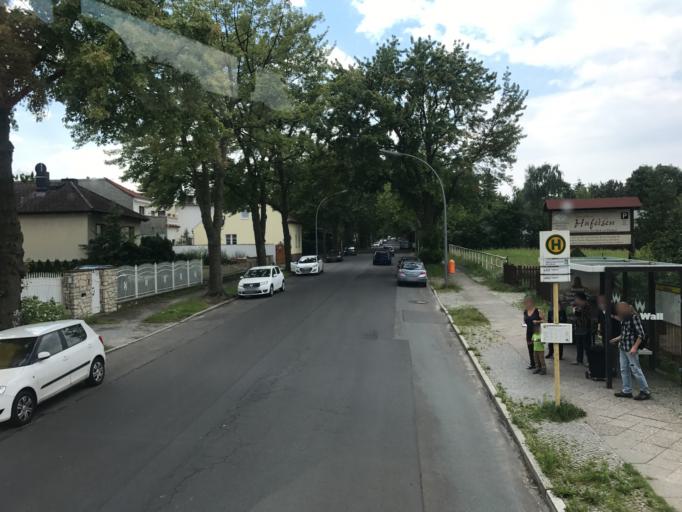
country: DE
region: Berlin
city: Lubars
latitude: 52.6176
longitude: 13.3531
